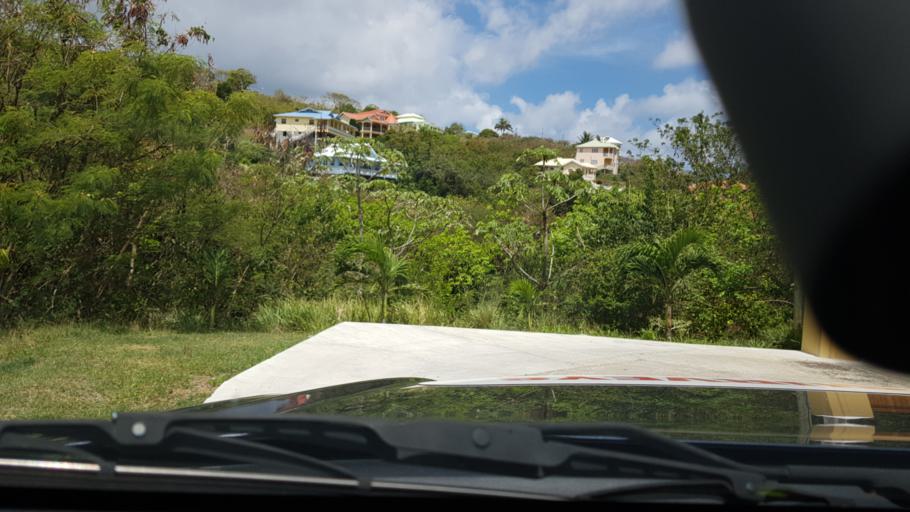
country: LC
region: Gros-Islet
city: Gros Islet
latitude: 14.0657
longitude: -60.9314
